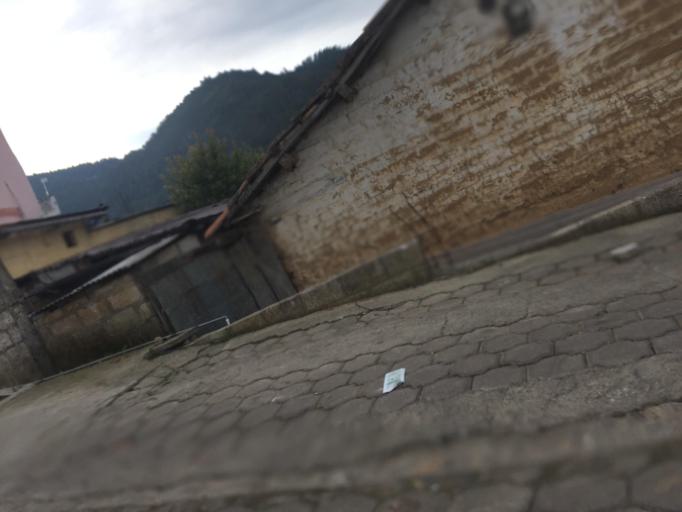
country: GT
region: Totonicapan
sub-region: Municipio de Totonicapan
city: Totonicapan
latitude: 14.9127
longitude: -91.3532
